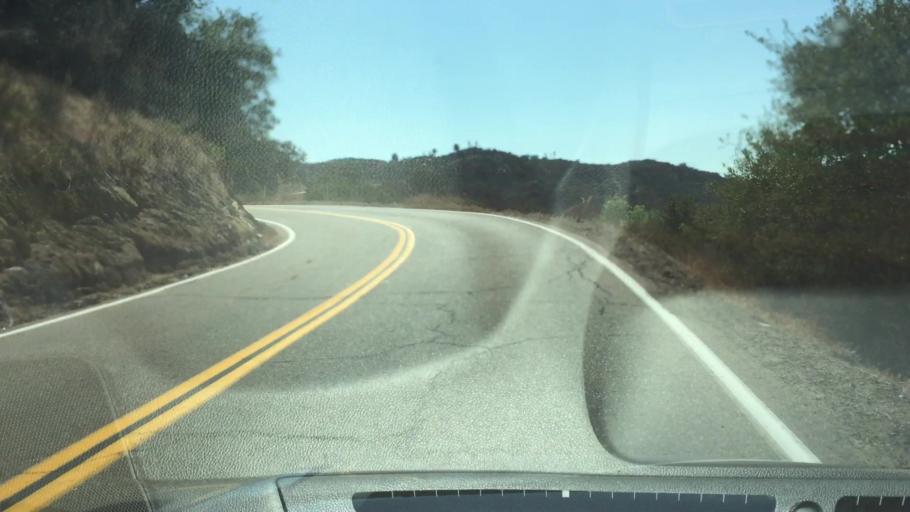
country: US
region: California
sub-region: San Diego County
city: Jamul
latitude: 32.7343
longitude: -116.8187
